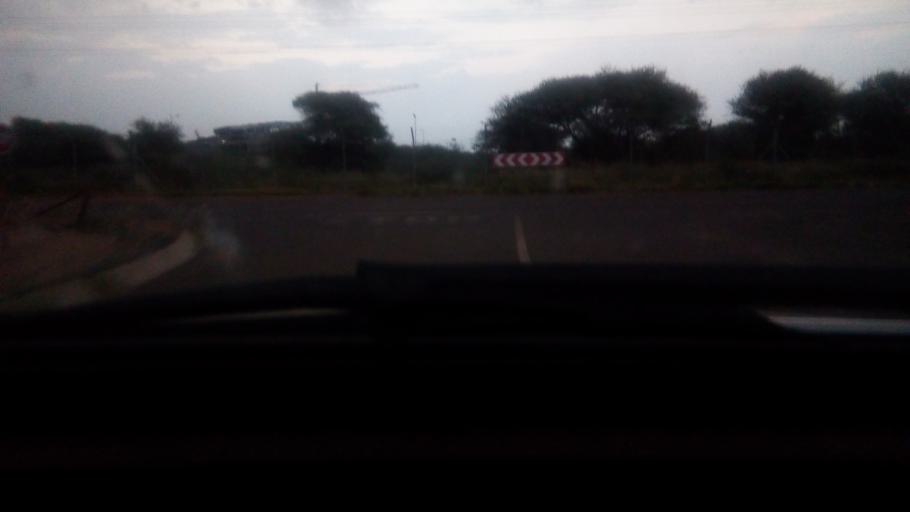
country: BW
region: Kweneng
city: Mmopone
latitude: -24.5881
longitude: 25.9118
